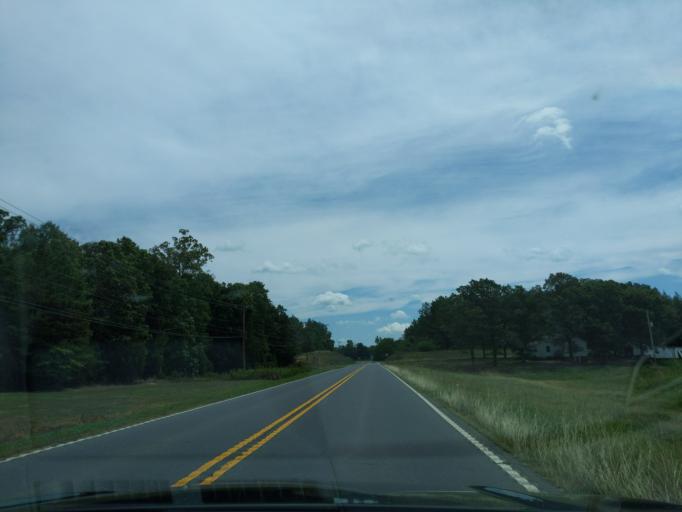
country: US
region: North Carolina
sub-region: Stanly County
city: Albemarle
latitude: 35.4694
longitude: -80.2774
